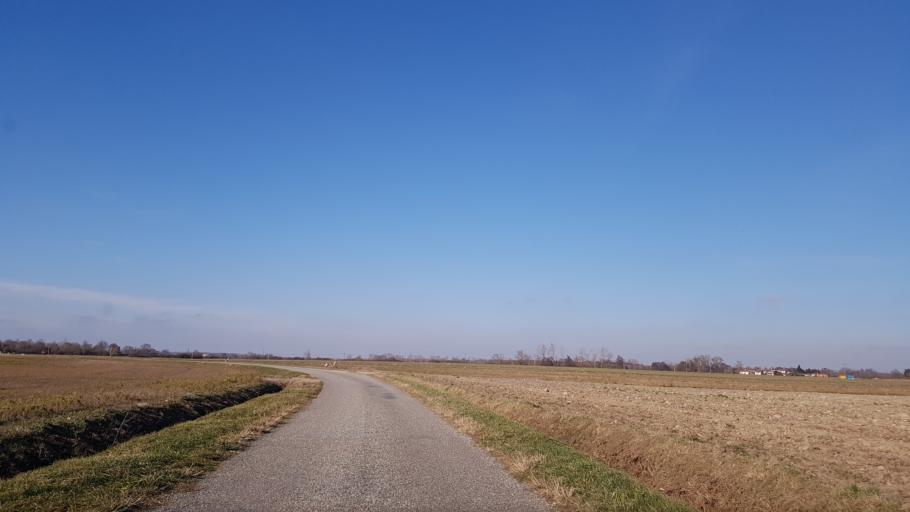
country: FR
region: Midi-Pyrenees
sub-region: Departement de l'Ariege
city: La Tour-du-Crieu
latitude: 43.1527
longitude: 1.6948
